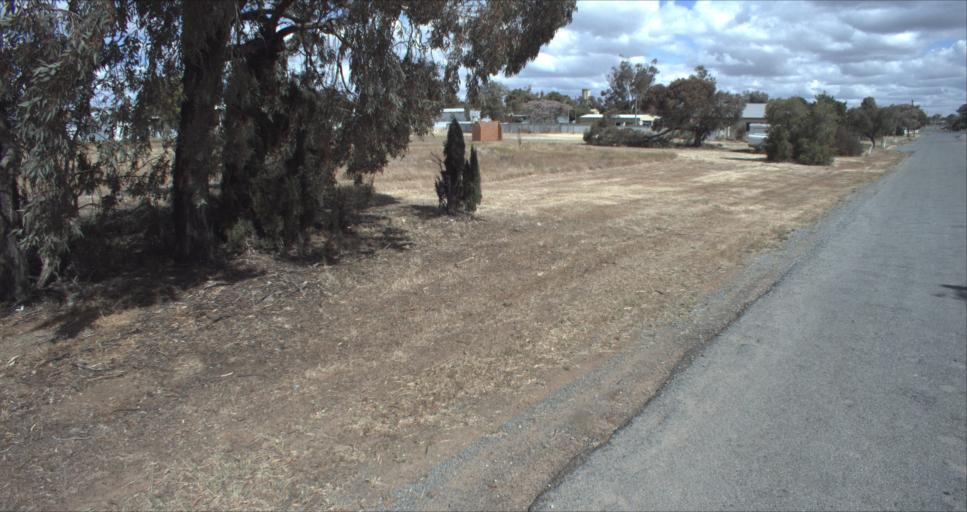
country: AU
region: New South Wales
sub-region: Leeton
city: Leeton
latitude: -34.5986
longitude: 146.4101
